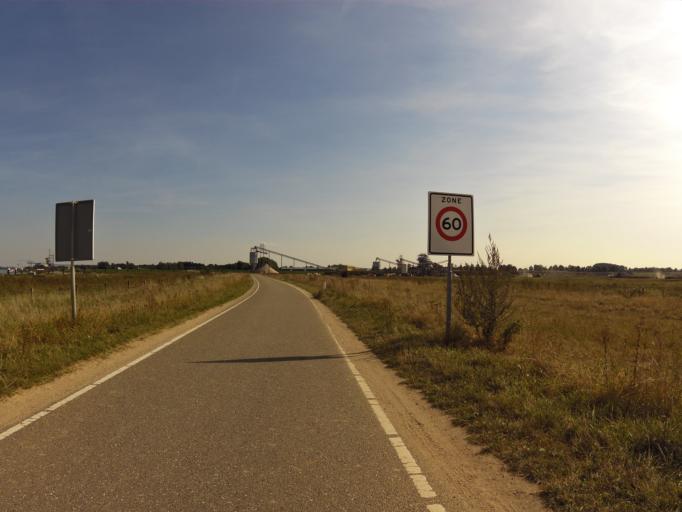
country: NL
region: Gelderland
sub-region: Gemeente Zevenaar
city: Zevenaar
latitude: 51.8748
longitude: 6.0250
